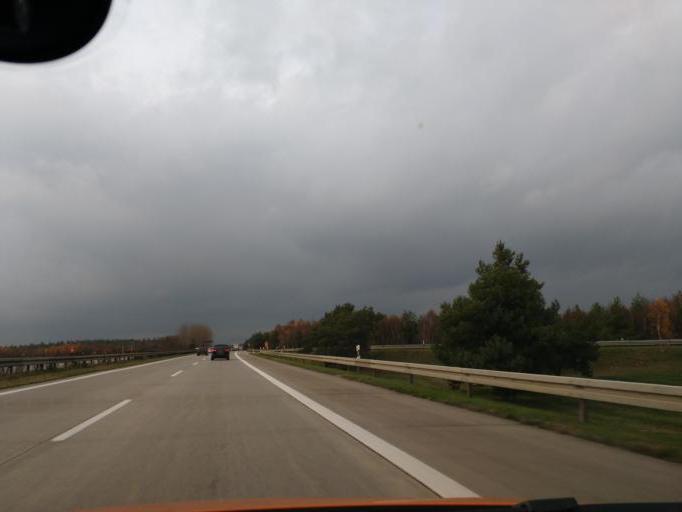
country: DE
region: Brandenburg
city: Heiligengrabe
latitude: 53.1502
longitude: 12.4050
